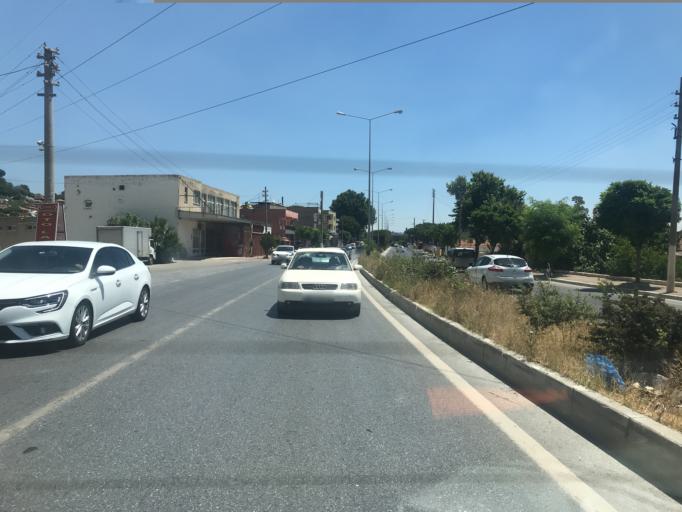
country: TR
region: Aydin
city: Soeke
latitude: 37.7829
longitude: 27.4592
